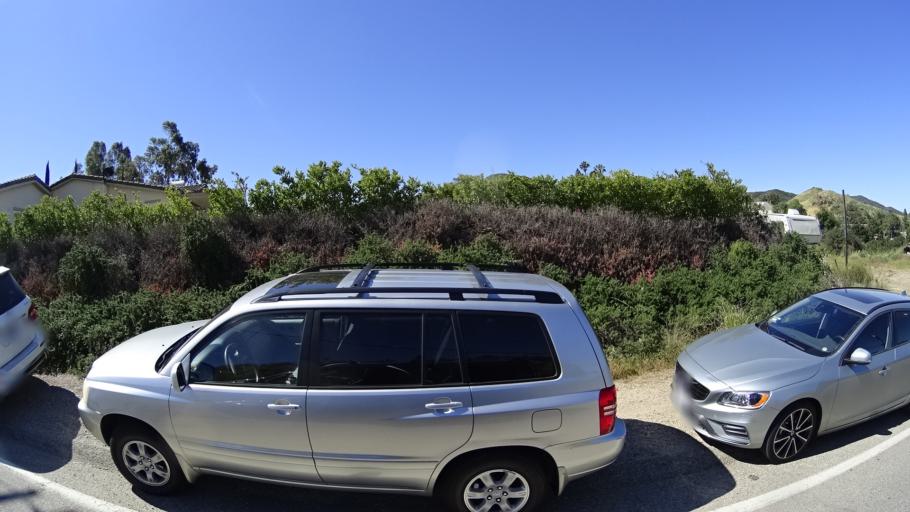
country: US
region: California
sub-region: Ventura County
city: Thousand Oaks
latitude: 34.1729
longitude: -118.8621
